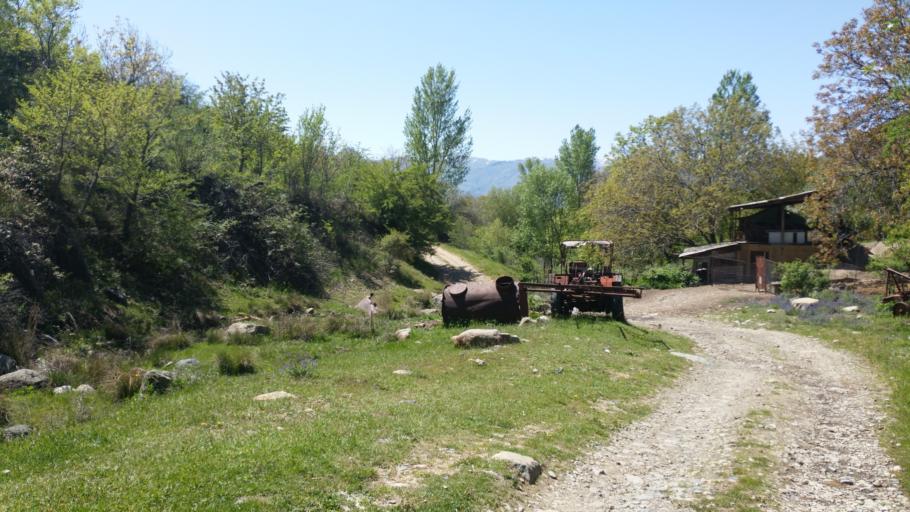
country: AM
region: Vayots' Dzori Marz
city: Vernashen
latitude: 39.7978
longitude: 45.3645
